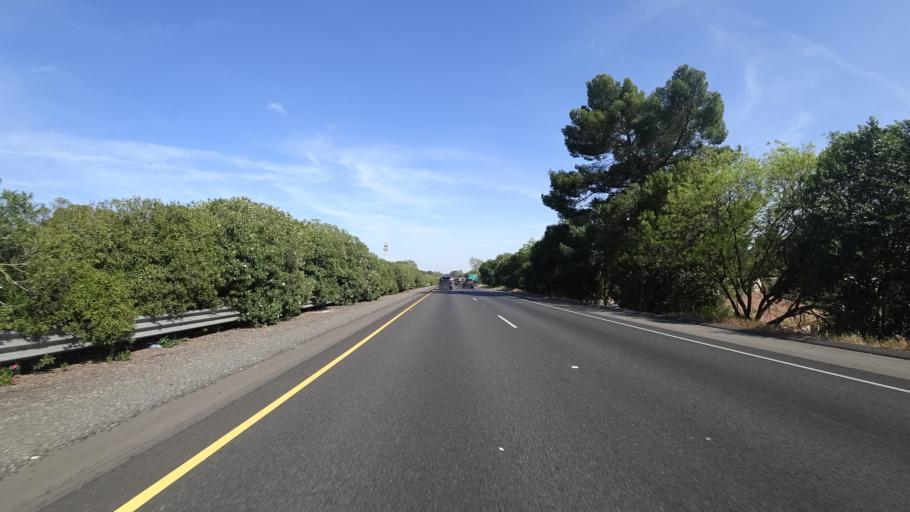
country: US
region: California
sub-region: Butte County
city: Chico
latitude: 39.7571
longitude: -121.8505
